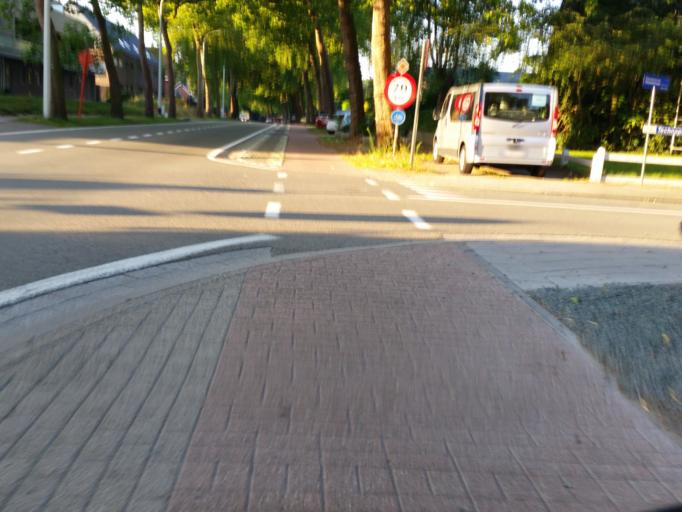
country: BE
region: Flanders
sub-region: Provincie Antwerpen
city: Mechelen
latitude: 51.0032
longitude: 4.4737
